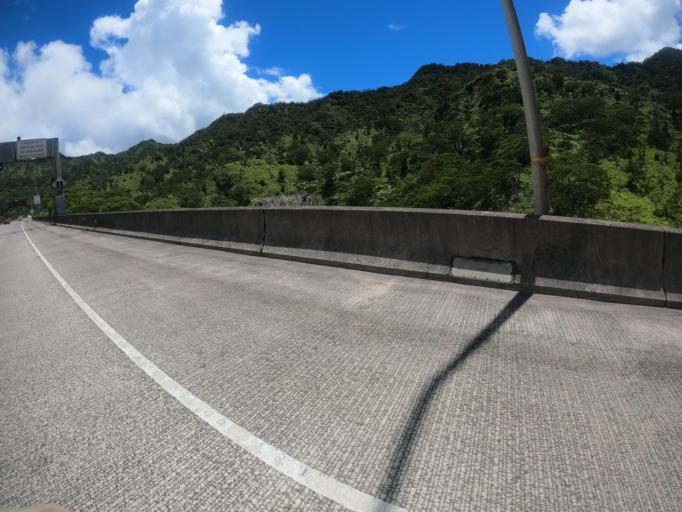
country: US
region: Hawaii
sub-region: Honolulu County
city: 'Ahuimanu
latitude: 21.4064
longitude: -157.8594
